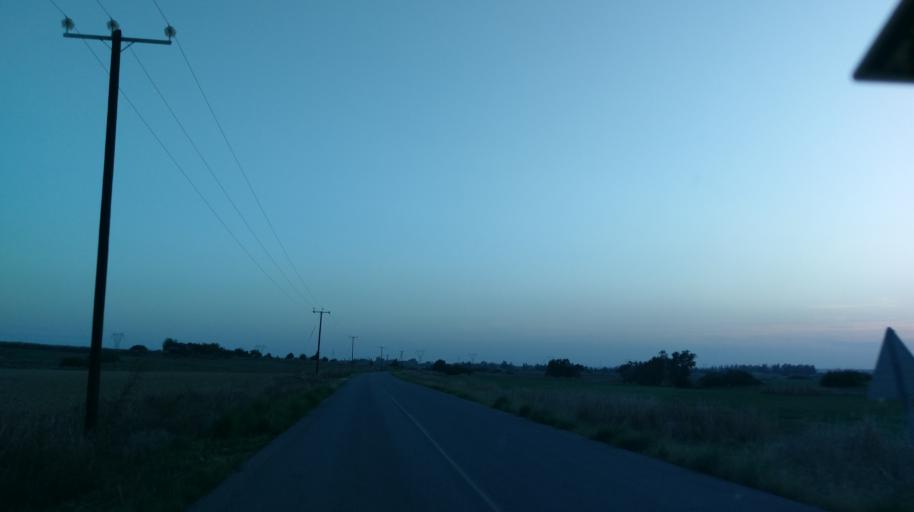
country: CY
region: Ammochostos
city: Trikomo
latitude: 35.3031
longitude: 33.8909
